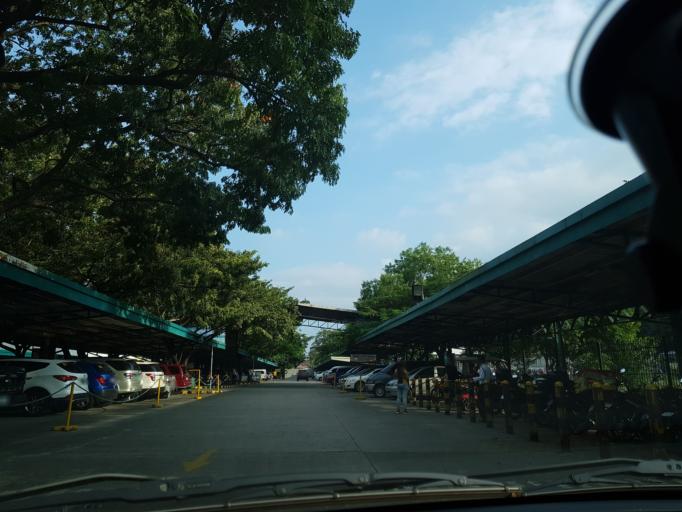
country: PH
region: Metro Manila
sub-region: City of Manila
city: Port Area
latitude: 14.5566
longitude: 120.9846
